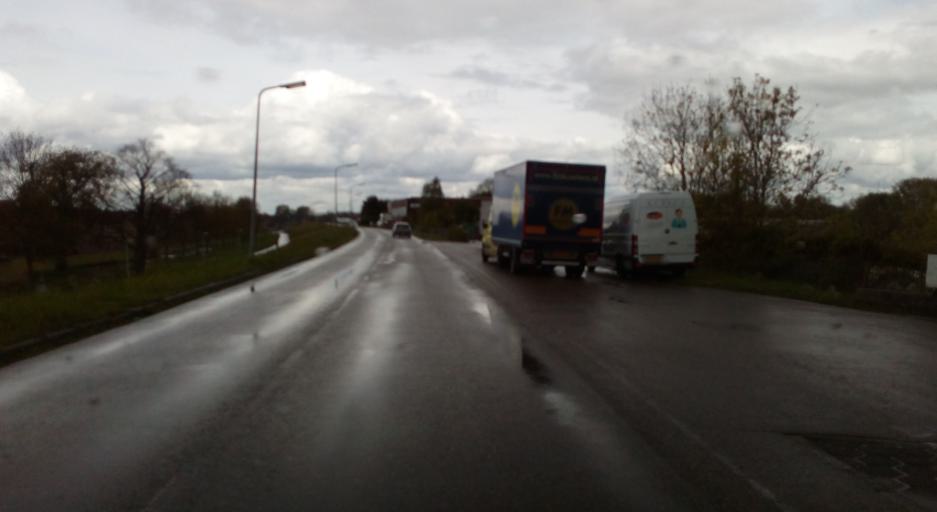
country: NL
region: South Holland
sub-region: Gemeente Dordrecht
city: Dordrecht
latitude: 51.8282
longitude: 4.6620
